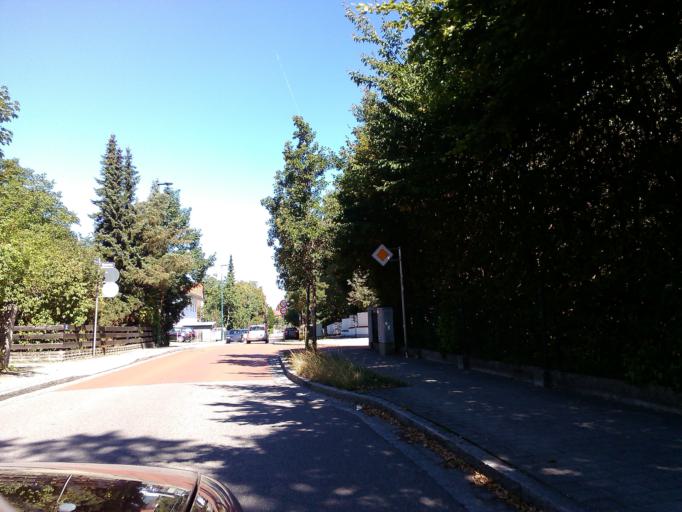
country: DE
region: Bavaria
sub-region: Upper Bavaria
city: Grafelfing
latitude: 48.1356
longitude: 11.4284
